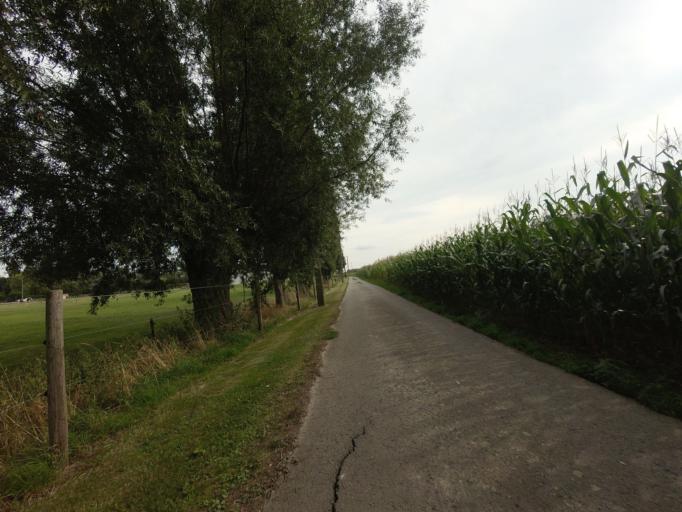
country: BE
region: Flanders
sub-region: Provincie Vlaams-Brabant
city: Meise
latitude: 50.9653
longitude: 4.3499
